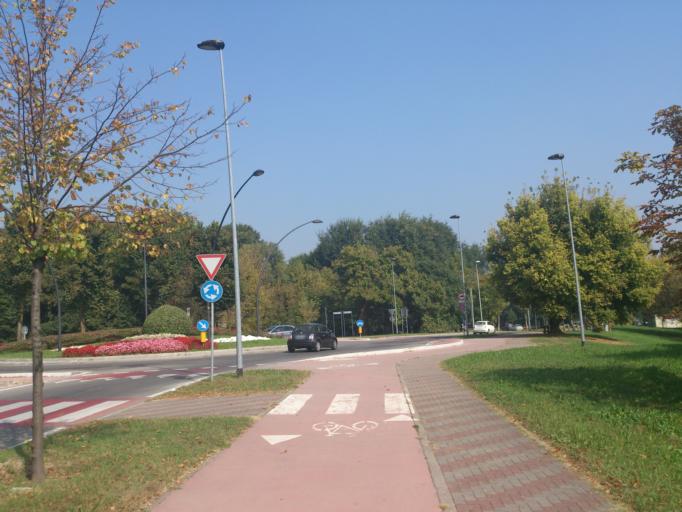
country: IT
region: Lombardy
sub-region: Citta metropolitana di Milano
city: San Donato Milanese
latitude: 45.4163
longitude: 9.2801
